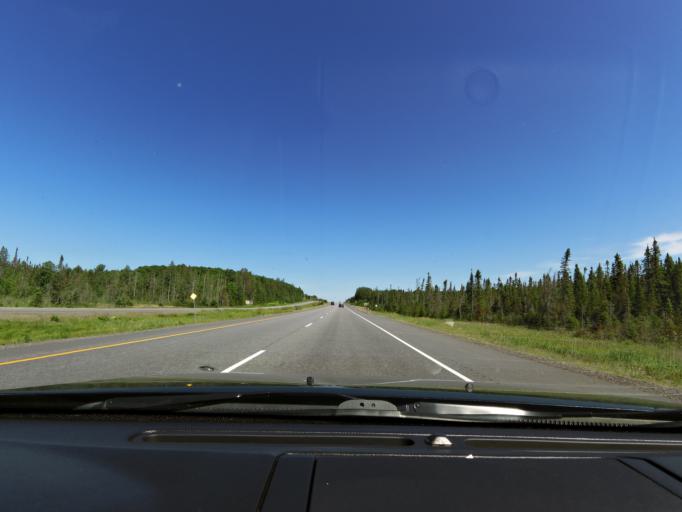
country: CA
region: Ontario
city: Huntsville
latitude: 45.4788
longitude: -79.2748
